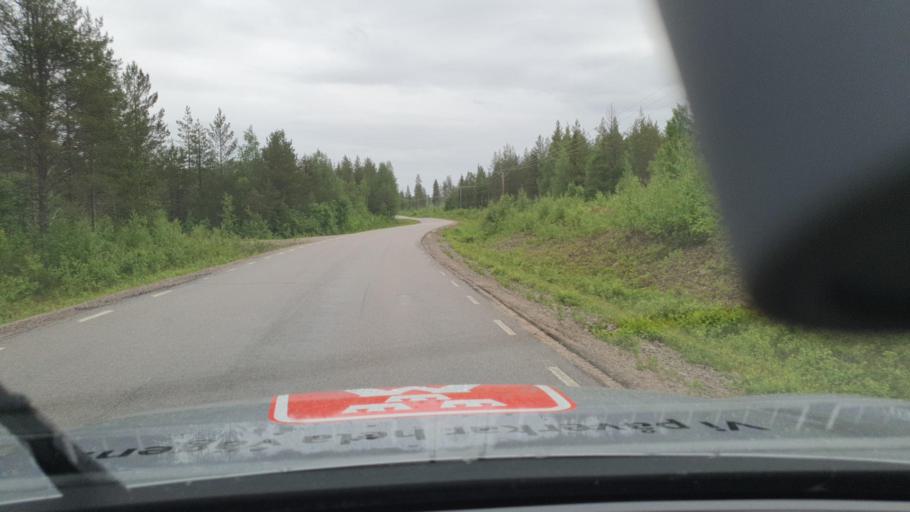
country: SE
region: Norrbotten
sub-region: Pajala Kommun
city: Pajala
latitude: 66.7636
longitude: 23.1543
